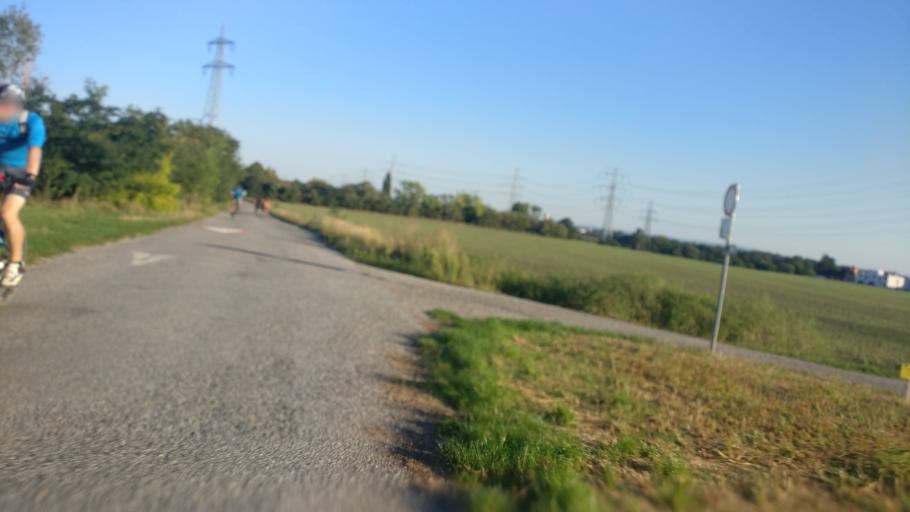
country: AT
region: Lower Austria
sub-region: Politischer Bezirk Wien-Umgebung
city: Lanzendorf
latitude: 48.1077
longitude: 16.4311
